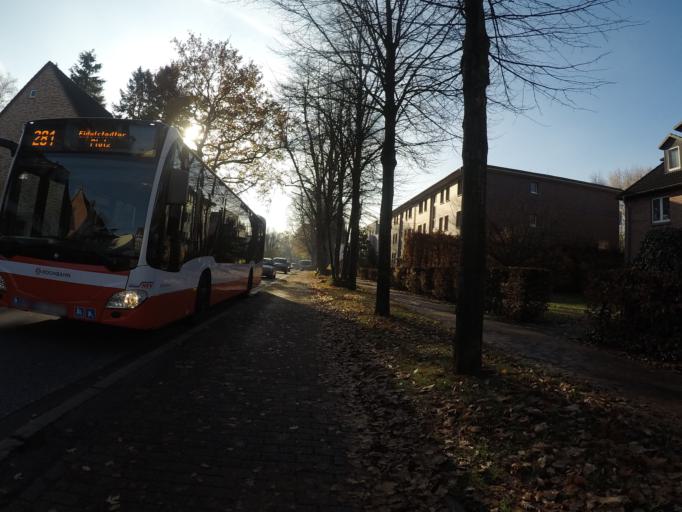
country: DE
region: Hamburg
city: Stellingen
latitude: 53.5962
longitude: 9.9327
